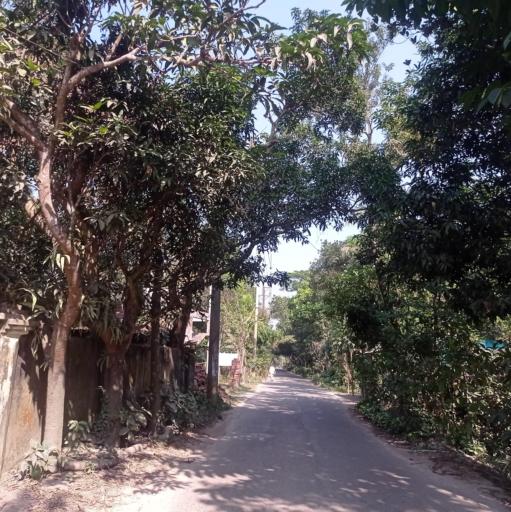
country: BD
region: Dhaka
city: Narsingdi
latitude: 24.0283
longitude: 90.6719
